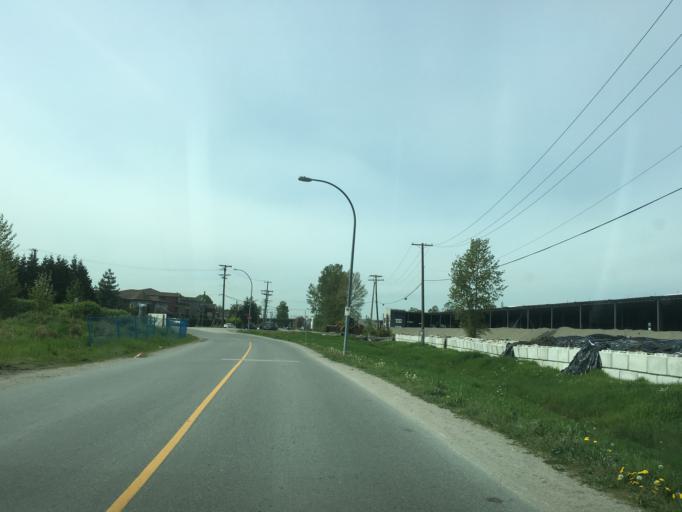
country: CA
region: British Columbia
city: New Westminster
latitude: 49.1952
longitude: -122.9361
